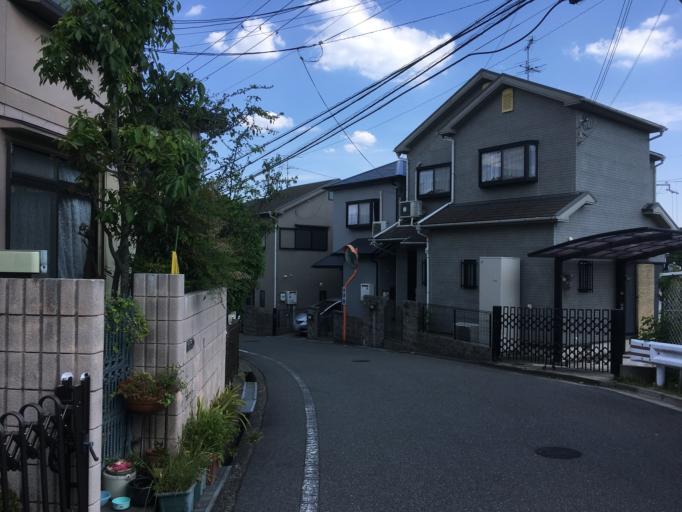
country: JP
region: Nara
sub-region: Ikoma-shi
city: Ikoma
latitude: 34.7014
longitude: 135.6933
